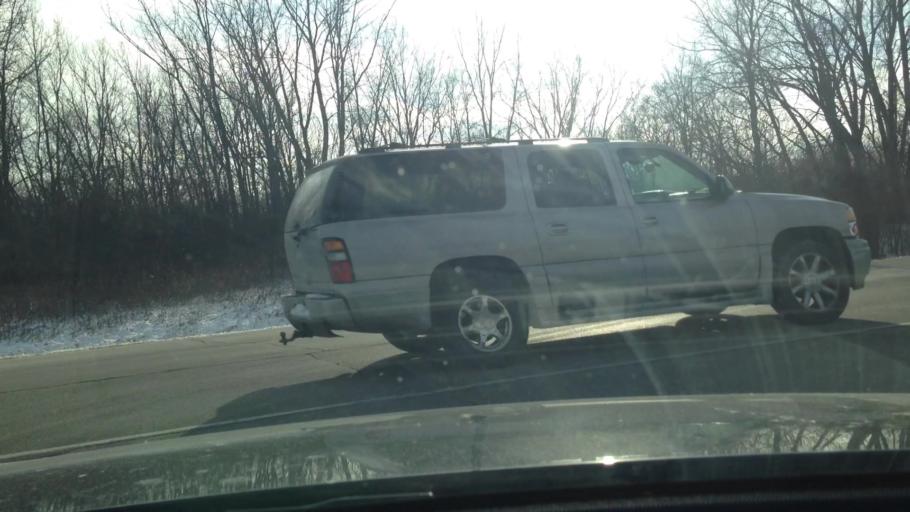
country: US
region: Wisconsin
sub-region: Waukesha County
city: Muskego
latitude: 42.9301
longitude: -88.1560
